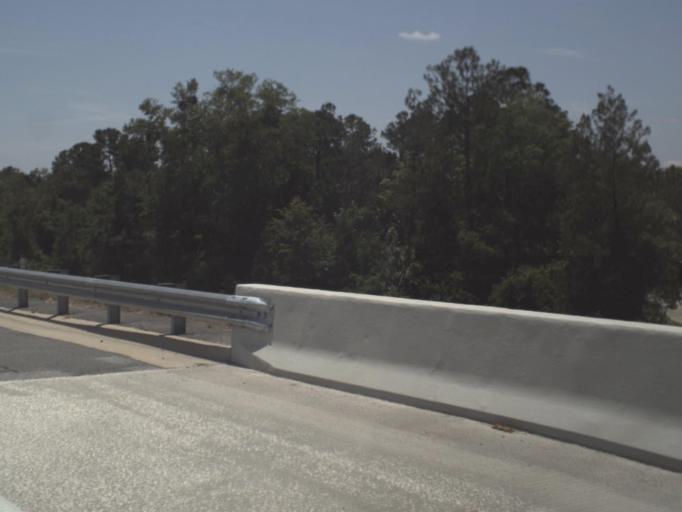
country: US
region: Florida
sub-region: Saint Johns County
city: Palm Valley
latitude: 30.1449
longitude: -81.5082
